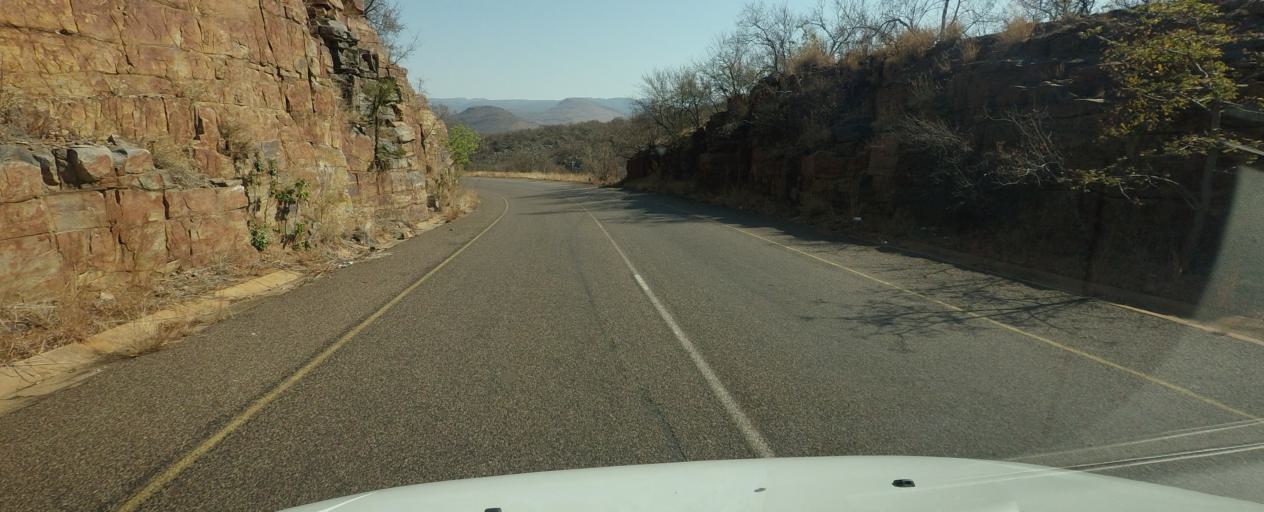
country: ZA
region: Limpopo
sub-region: Mopani District Municipality
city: Hoedspruit
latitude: -24.5562
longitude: 30.7371
